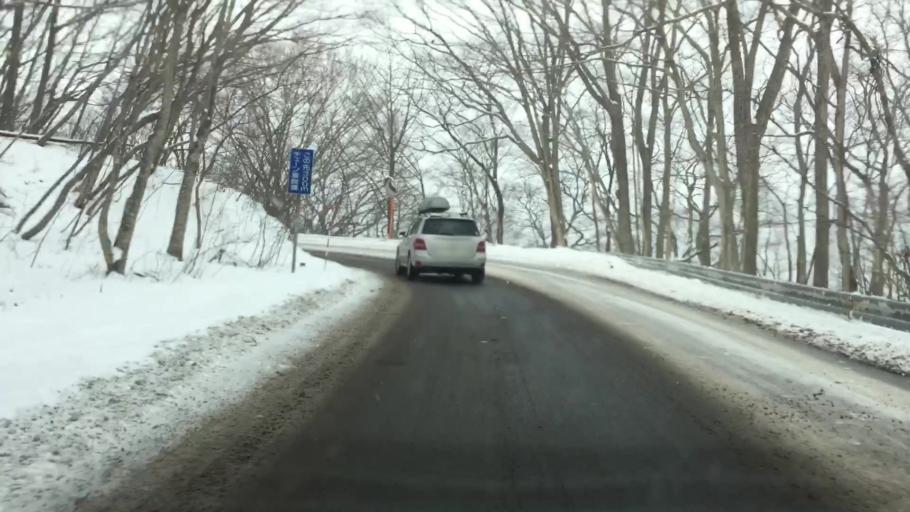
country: JP
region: Tochigi
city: Yaita
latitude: 36.9696
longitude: 139.7900
